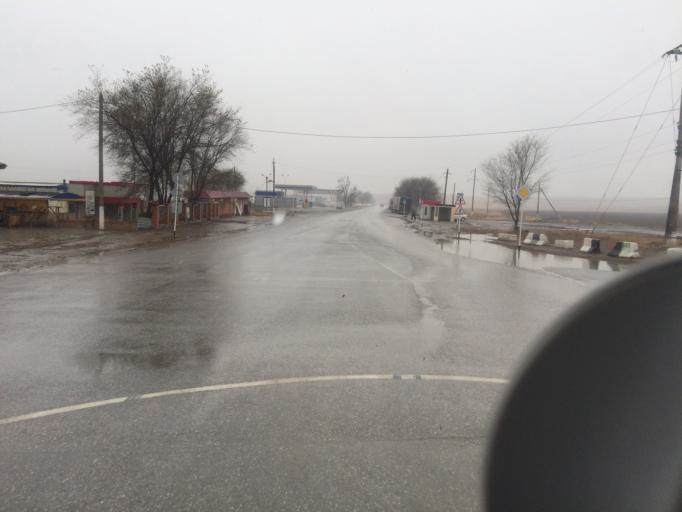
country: KG
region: Chuy
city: Kant
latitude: 43.0011
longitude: 74.8669
